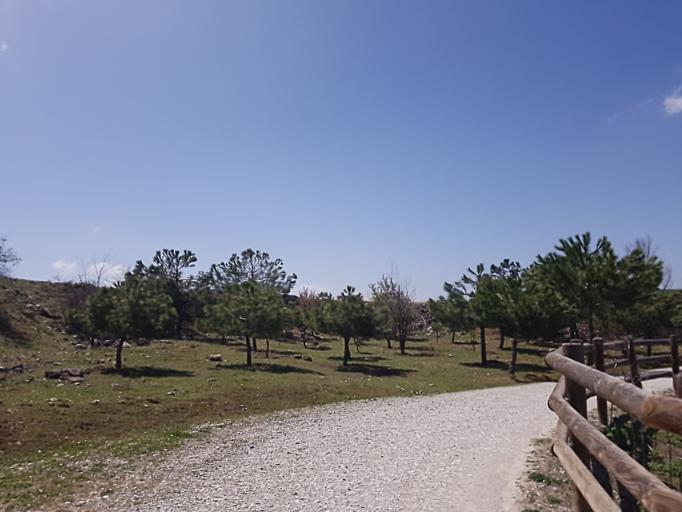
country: ES
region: Castille and Leon
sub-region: Provincia de Segovia
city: Segovia
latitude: 40.9464
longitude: -4.1319
